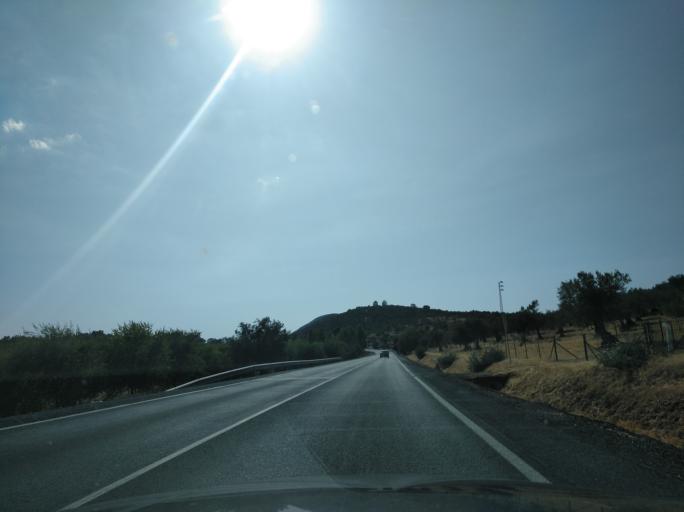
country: ES
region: Andalusia
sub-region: Provincia de Huelva
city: Rosal de la Frontera
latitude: 37.9655
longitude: -7.2307
